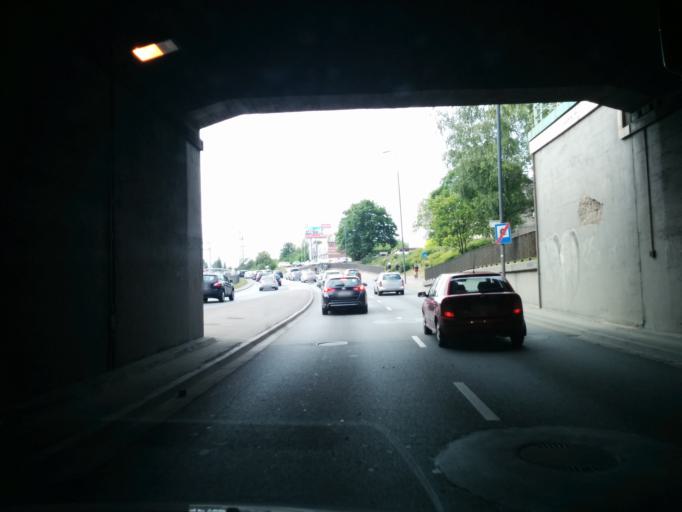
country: PL
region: Masovian Voivodeship
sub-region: Warszawa
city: Ochota
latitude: 52.2179
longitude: 20.9601
